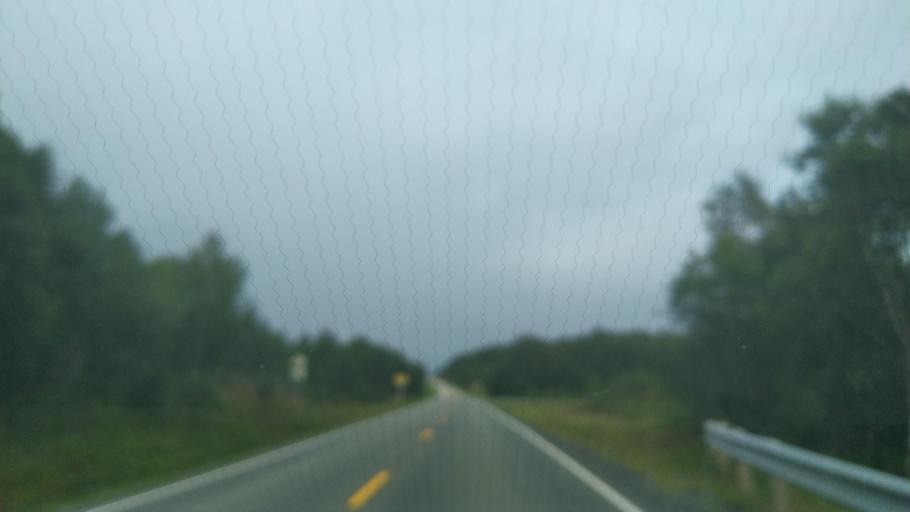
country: NO
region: Nordland
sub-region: Evenes
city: Randa
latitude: 68.4992
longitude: 16.8467
